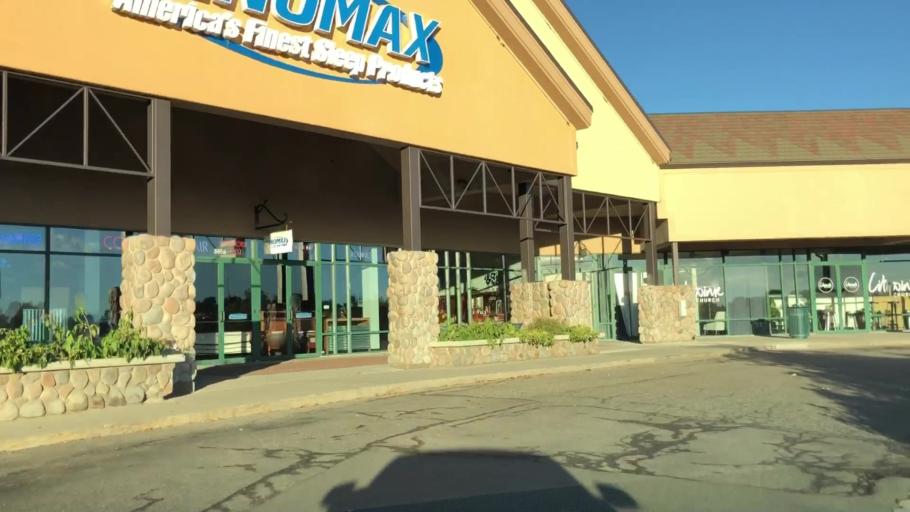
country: US
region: Colorado
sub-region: Larimer County
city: Loveland
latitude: 40.4091
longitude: -104.9965
